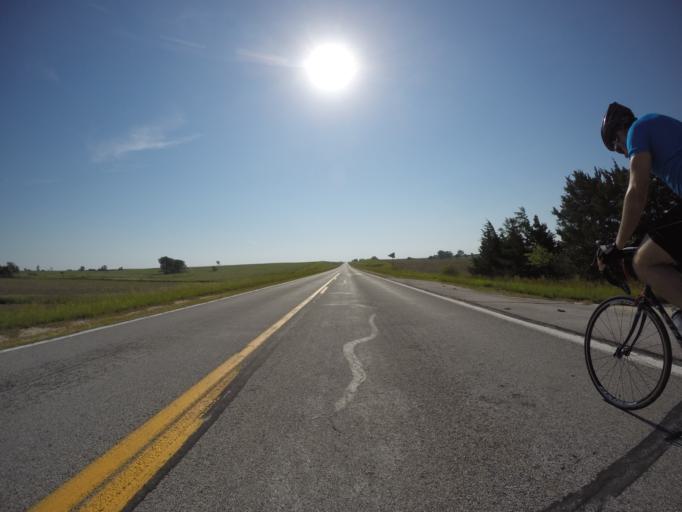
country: US
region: Nebraska
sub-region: Pawnee County
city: Pawnee City
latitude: 40.0447
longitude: -96.3680
